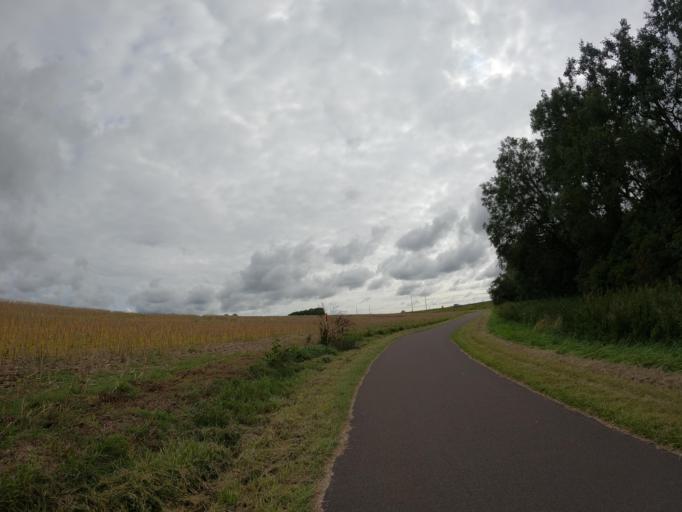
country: DE
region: Mecklenburg-Vorpommern
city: Samtens
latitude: 54.3555
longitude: 13.2639
